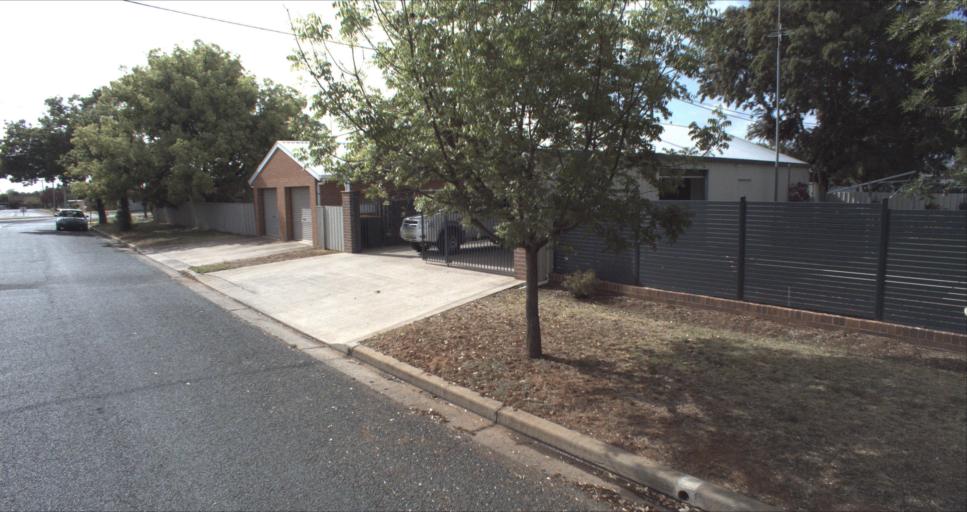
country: AU
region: New South Wales
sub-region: Leeton
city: Leeton
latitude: -34.5604
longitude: 146.4103
